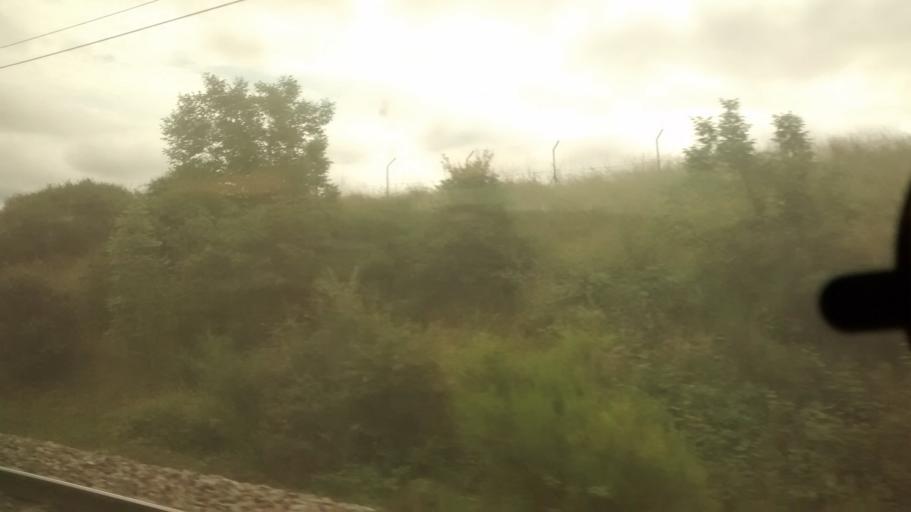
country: FR
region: Centre
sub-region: Departement d'Eure-et-Loir
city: Aunay-sous-Auneau
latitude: 48.4473
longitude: 1.7889
